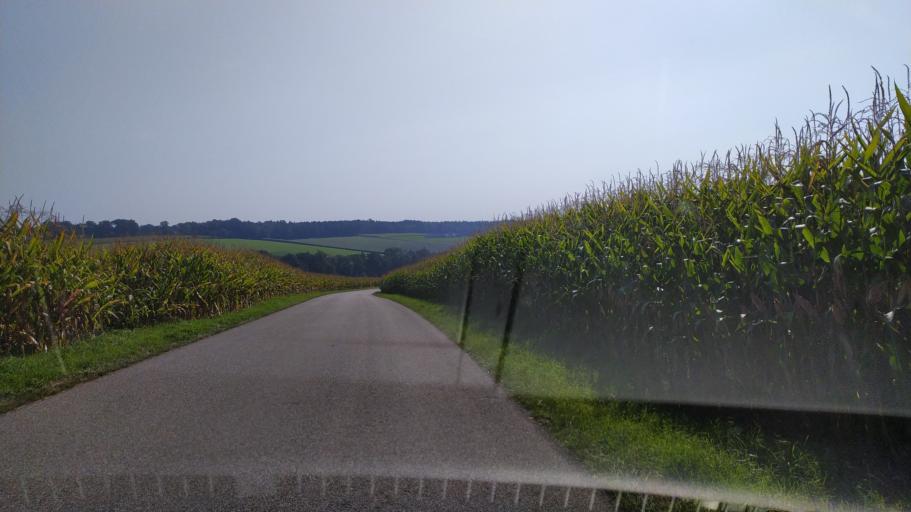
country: AT
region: Lower Austria
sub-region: Politischer Bezirk Amstetten
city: Zeillern
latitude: 48.1111
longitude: 14.7416
